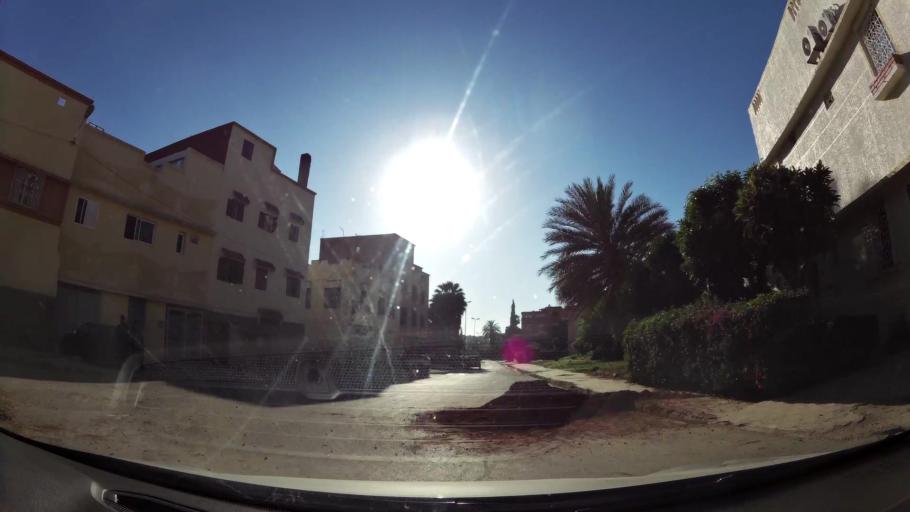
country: MA
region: Meknes-Tafilalet
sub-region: Meknes
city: Meknes
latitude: 33.8778
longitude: -5.5637
